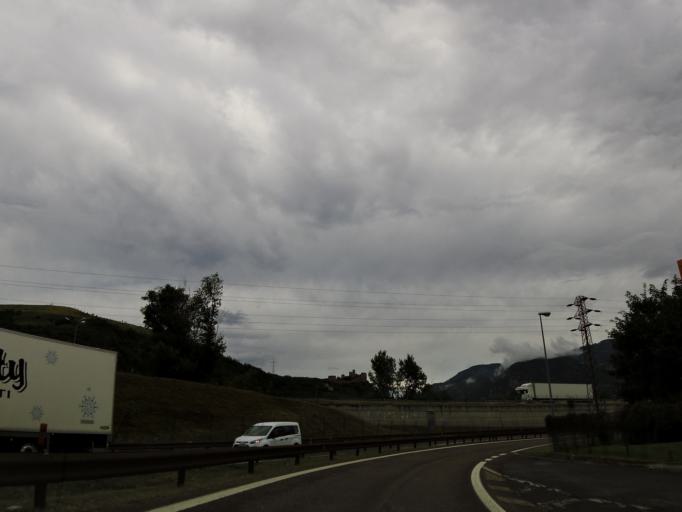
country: IT
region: Trentino-Alto Adige
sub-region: Bolzano
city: San Giacomo
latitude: 46.4732
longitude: 11.3132
